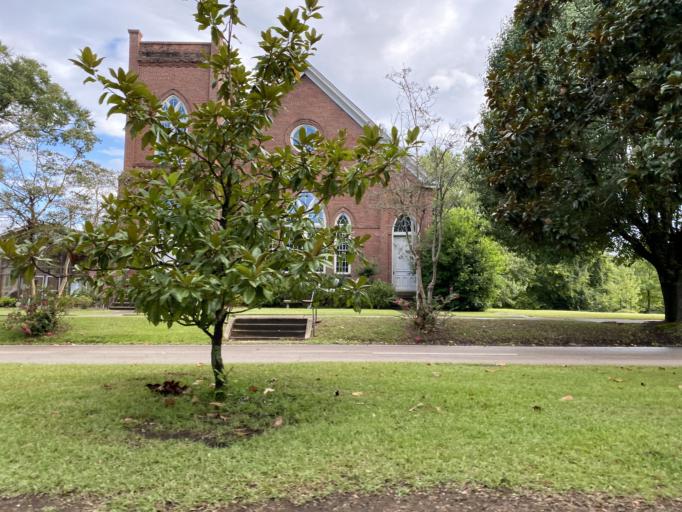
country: US
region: Mississippi
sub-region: Monroe County
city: Aberdeen
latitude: 33.8254
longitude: -88.5478
